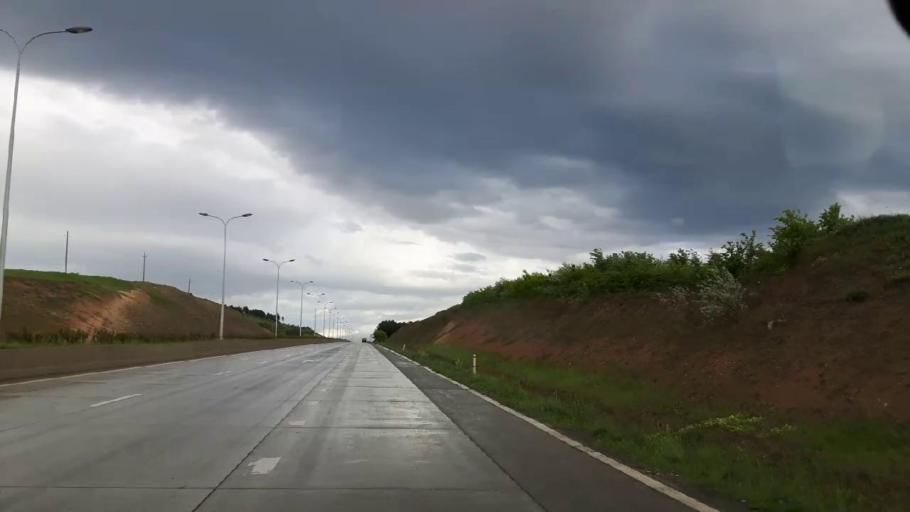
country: GE
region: Shida Kartli
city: Gori
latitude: 42.0123
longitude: 44.0368
